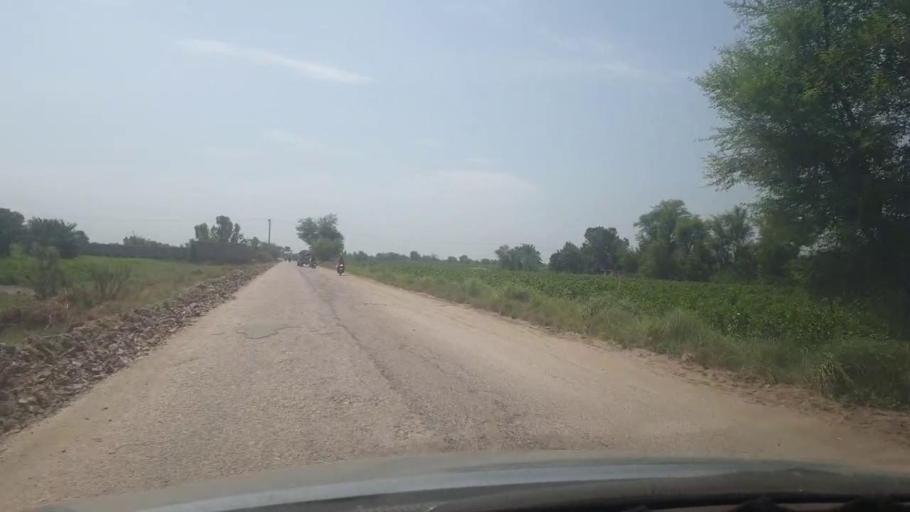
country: PK
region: Sindh
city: Bozdar
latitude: 27.2186
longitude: 68.5689
